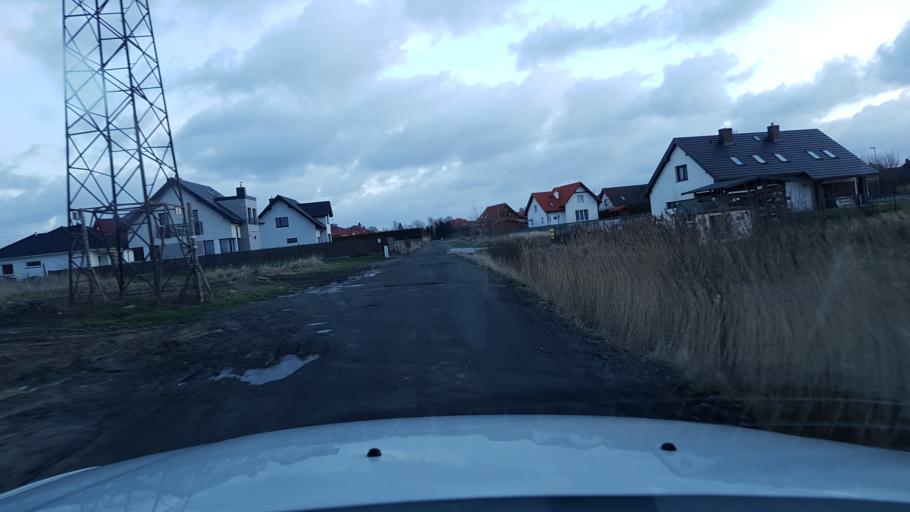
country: PL
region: West Pomeranian Voivodeship
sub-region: Powiat kolobrzeski
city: Kolobrzeg
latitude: 54.1529
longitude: 15.5549
